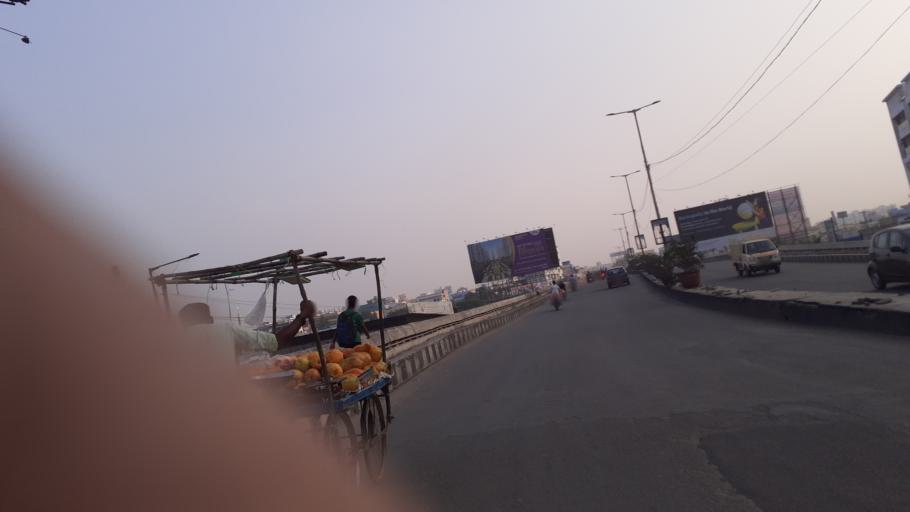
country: IN
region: Telangana
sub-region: Rangareddi
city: Kukatpalli
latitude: 17.4844
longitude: 78.3603
